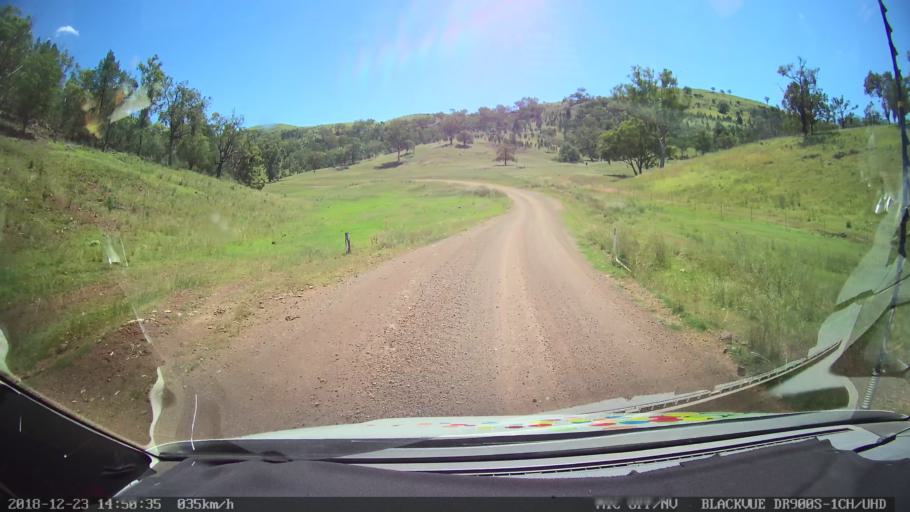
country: AU
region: New South Wales
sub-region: Tamworth Municipality
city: Manilla
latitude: -30.6721
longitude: 150.8567
